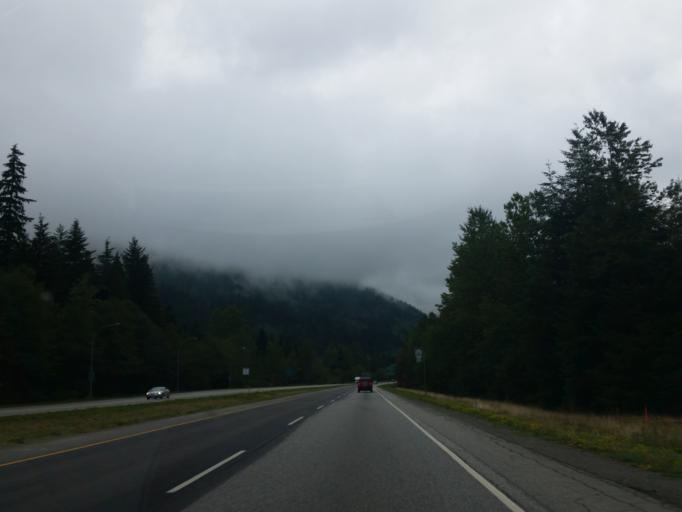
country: CA
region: British Columbia
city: Hope
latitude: 49.4669
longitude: -121.2541
